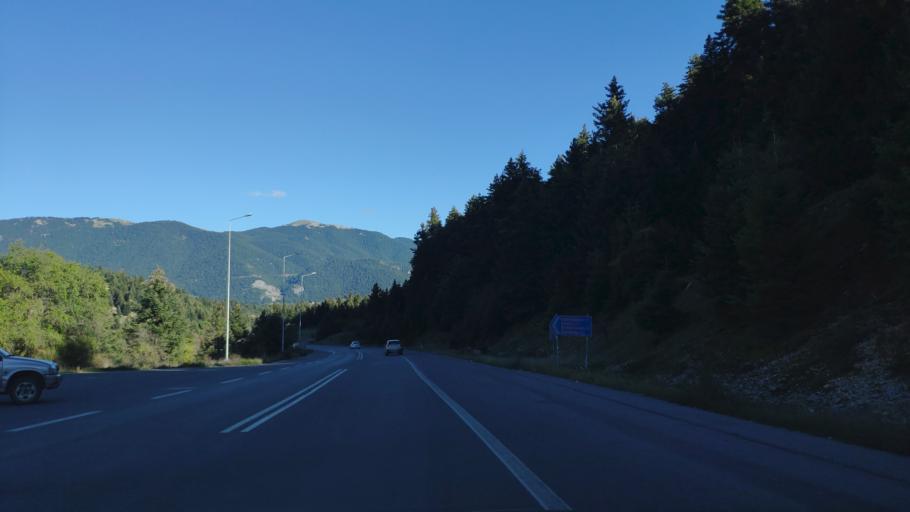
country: GR
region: Peloponnese
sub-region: Nomos Arkadias
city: Langadhia
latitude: 37.6561
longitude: 22.1455
